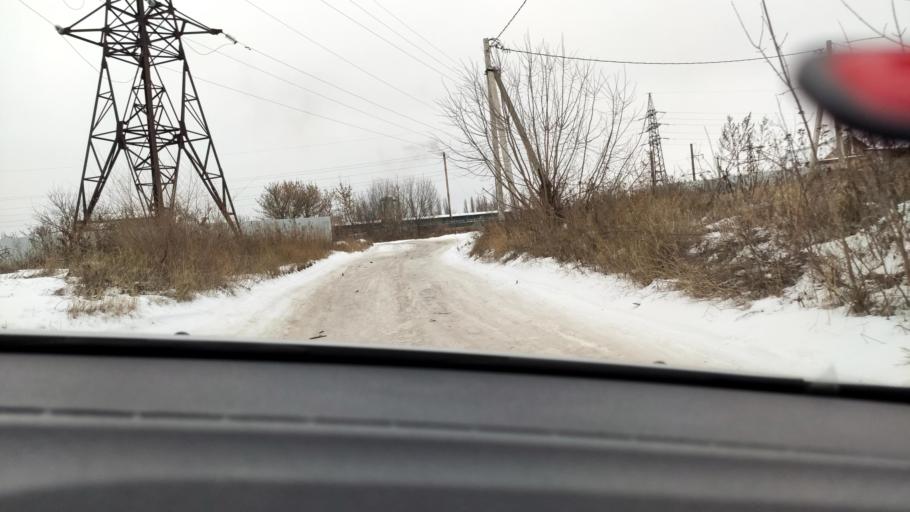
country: RU
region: Voronezj
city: Semiluki
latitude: 51.6945
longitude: 38.9938
